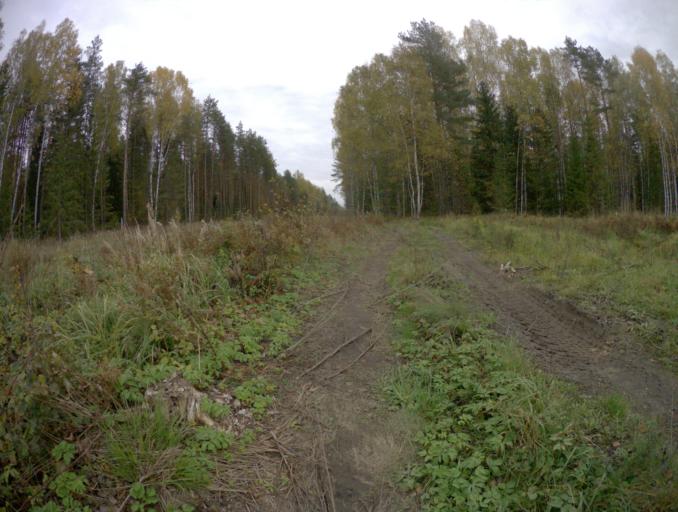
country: RU
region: Vladimir
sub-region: Kovrovskiy Rayon
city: Kovrov
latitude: 56.3150
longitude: 41.5383
